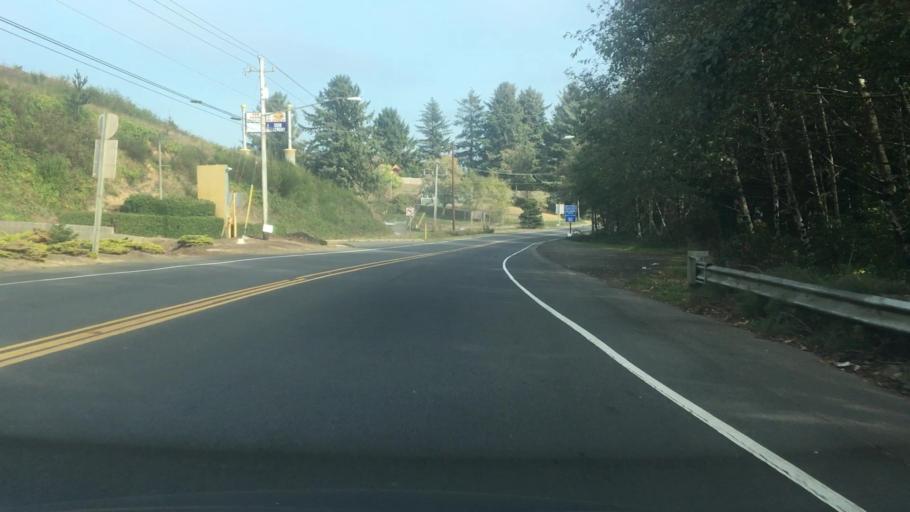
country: US
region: Oregon
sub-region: Lincoln County
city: Lincoln City
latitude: 44.9967
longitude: -124.0029
